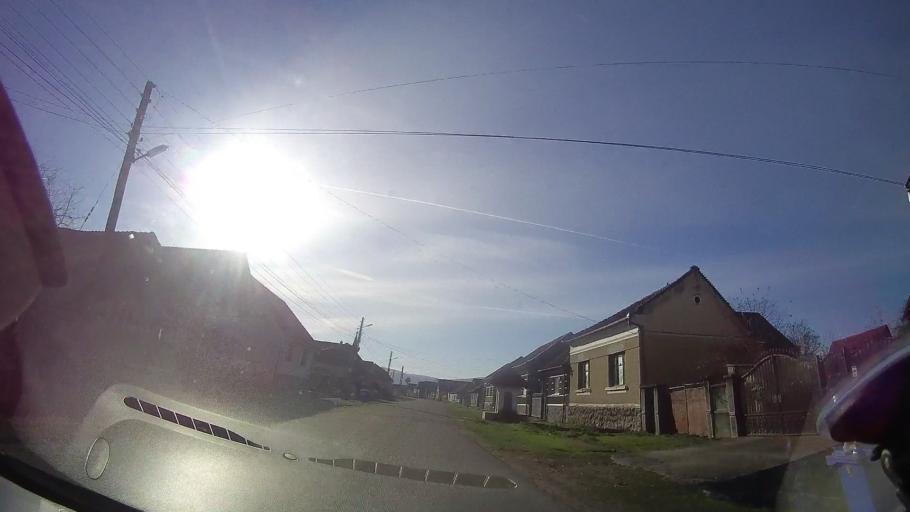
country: RO
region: Bihor
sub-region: Comuna Auseu
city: Grosi
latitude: 47.0247
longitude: 22.4729
